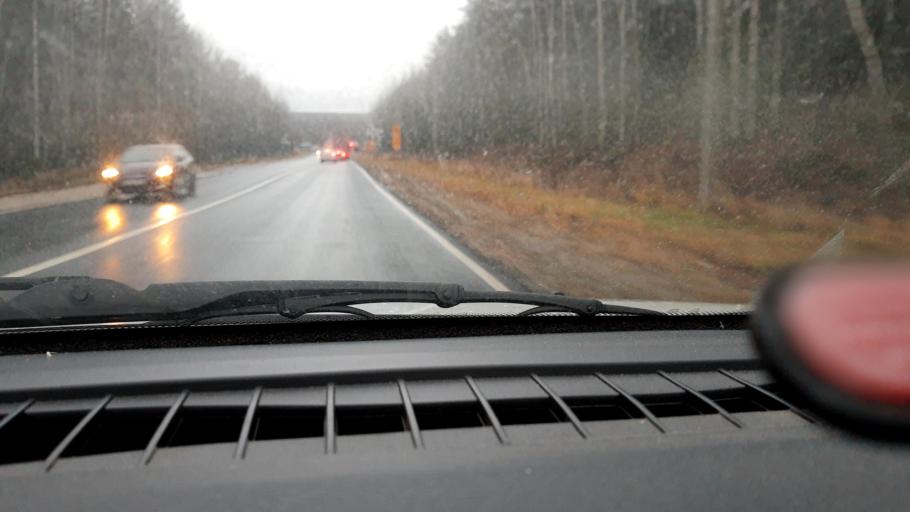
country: RU
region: Nizjnij Novgorod
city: Krasnyye Baki
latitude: 57.1043
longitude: 45.1852
